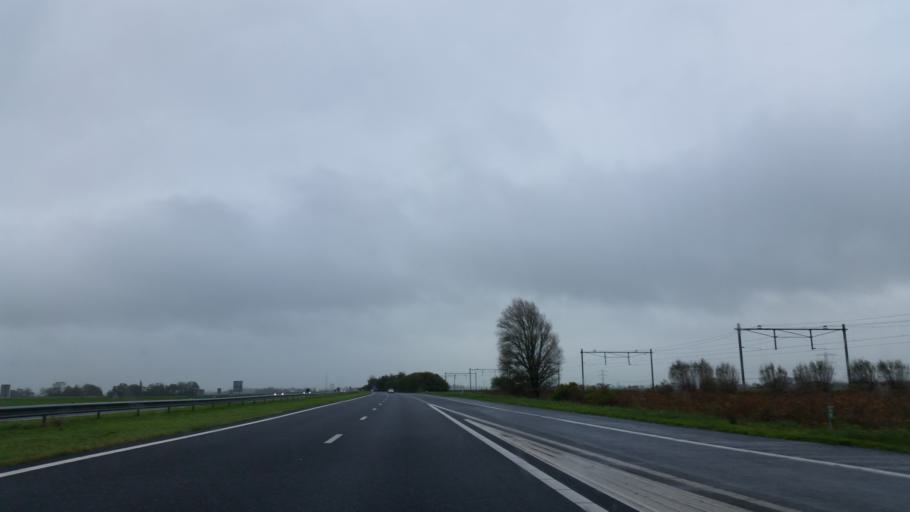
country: NL
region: Friesland
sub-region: Gemeente Leeuwarden
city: Wirdum
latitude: 53.1432
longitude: 5.7969
